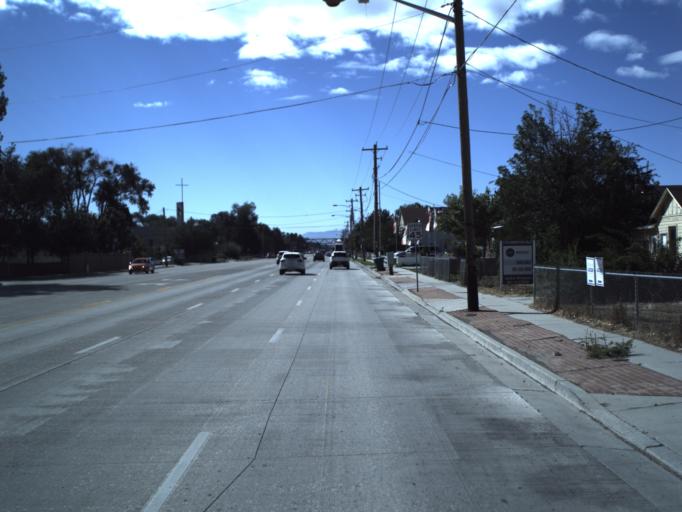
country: US
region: Utah
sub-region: Salt Lake County
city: West Jordan
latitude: 40.6190
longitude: -111.9389
